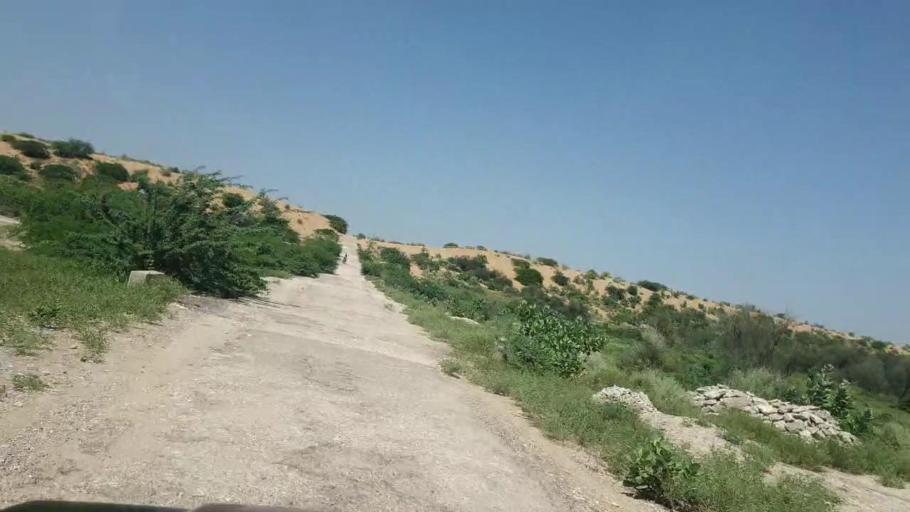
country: PK
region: Sindh
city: Chor
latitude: 25.3493
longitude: 70.3468
